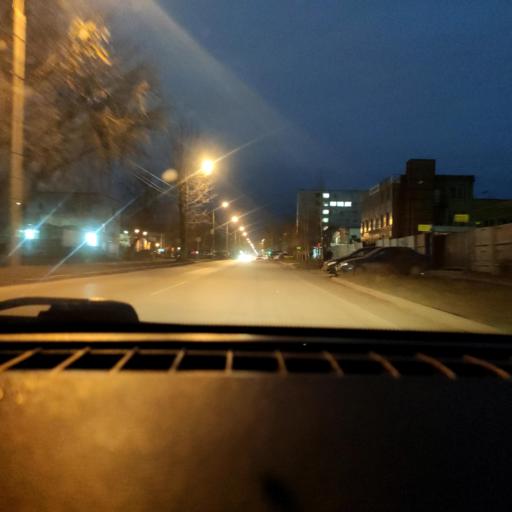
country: RU
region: Perm
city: Perm
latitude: 57.9666
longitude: 56.2203
